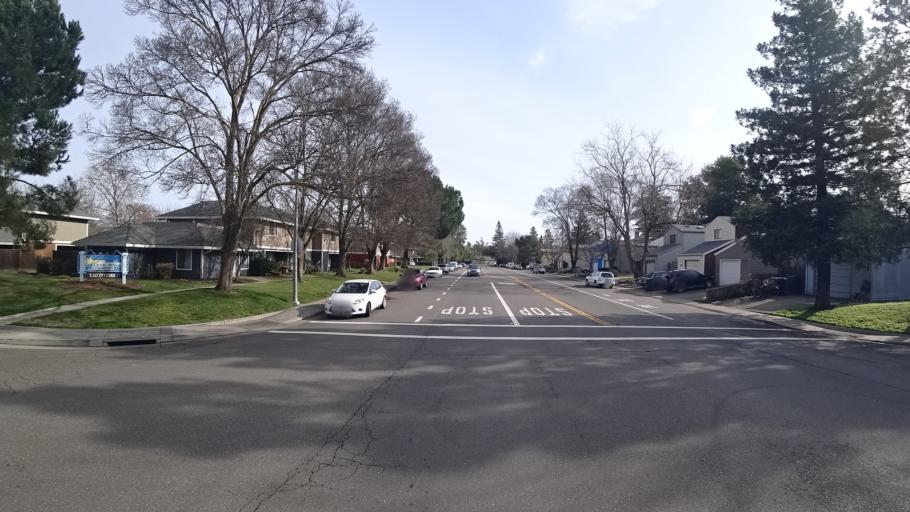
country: US
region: California
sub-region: Yolo County
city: Davis
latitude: 38.5479
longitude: -121.6996
